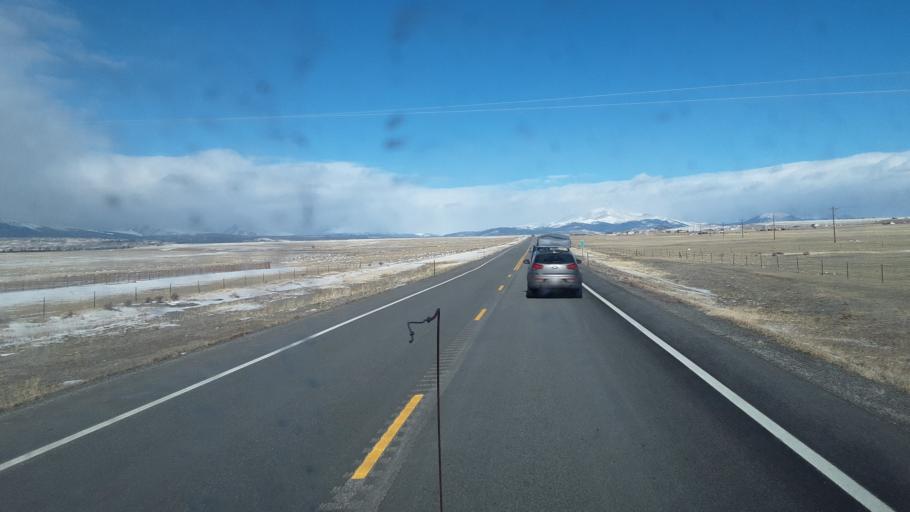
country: US
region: Colorado
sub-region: Park County
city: Fairplay
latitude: 39.1055
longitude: -105.9902
